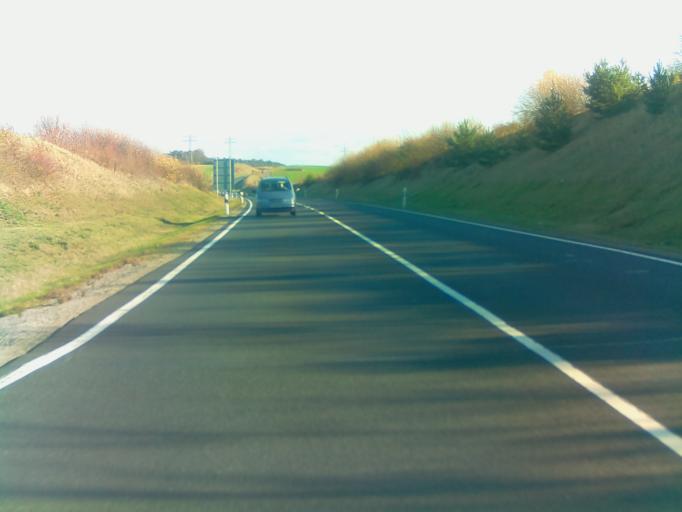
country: DE
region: Bavaria
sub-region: Regierungsbezirk Unterfranken
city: Rodelmaier
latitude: 50.3289
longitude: 10.2736
